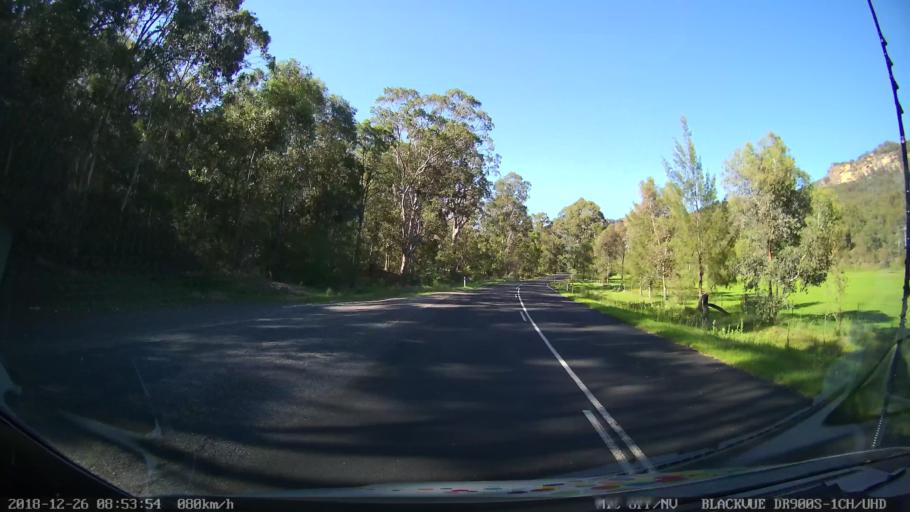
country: AU
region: New South Wales
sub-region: Mid-Western Regional
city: Kandos
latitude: -32.6093
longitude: 150.0755
